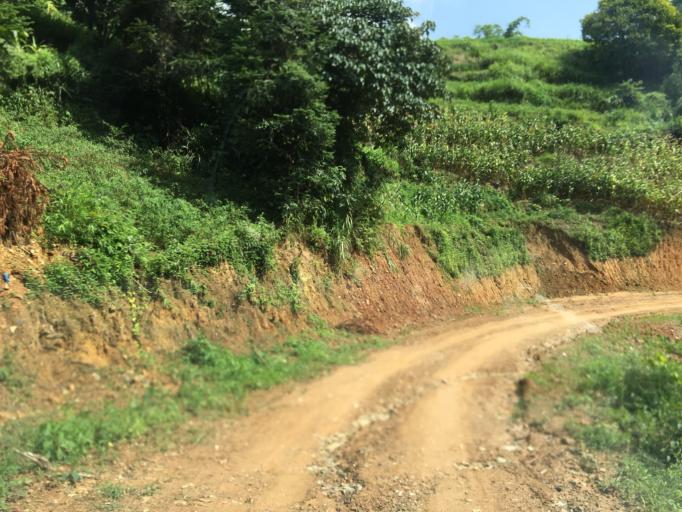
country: CN
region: Guangxi Zhuangzu Zizhiqu
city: Xinzhou
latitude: 24.8679
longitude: 105.8585
